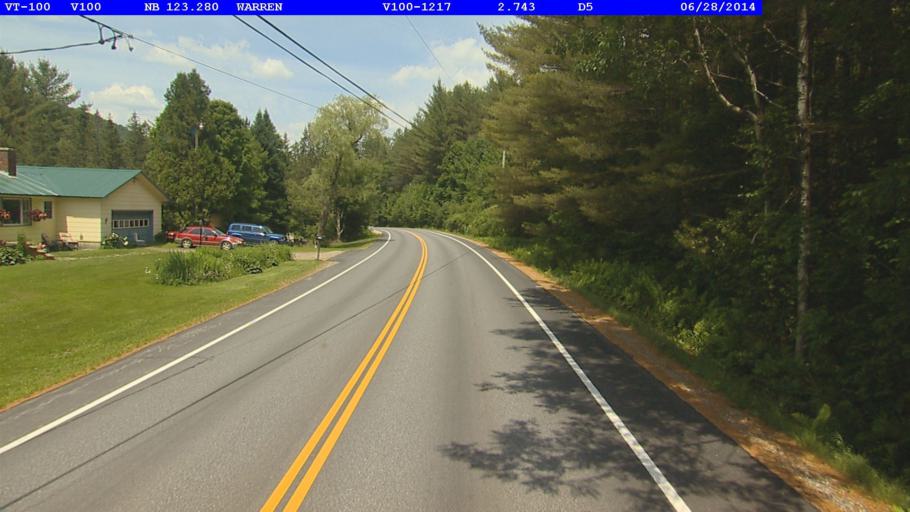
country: US
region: Vermont
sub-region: Washington County
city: Northfield
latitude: 44.0981
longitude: -72.8615
